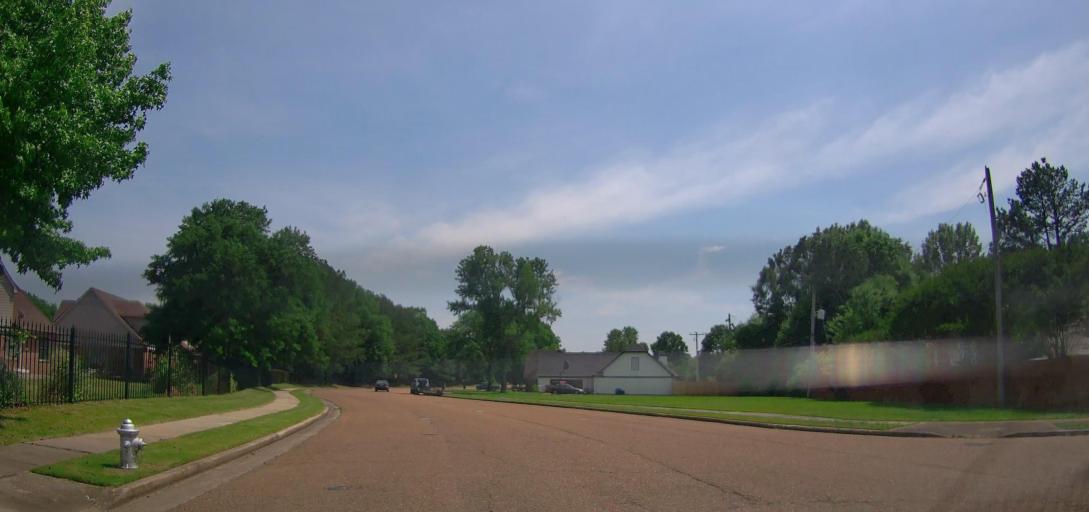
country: US
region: Tennessee
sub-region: Shelby County
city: Germantown
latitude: 35.0421
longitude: -89.7874
